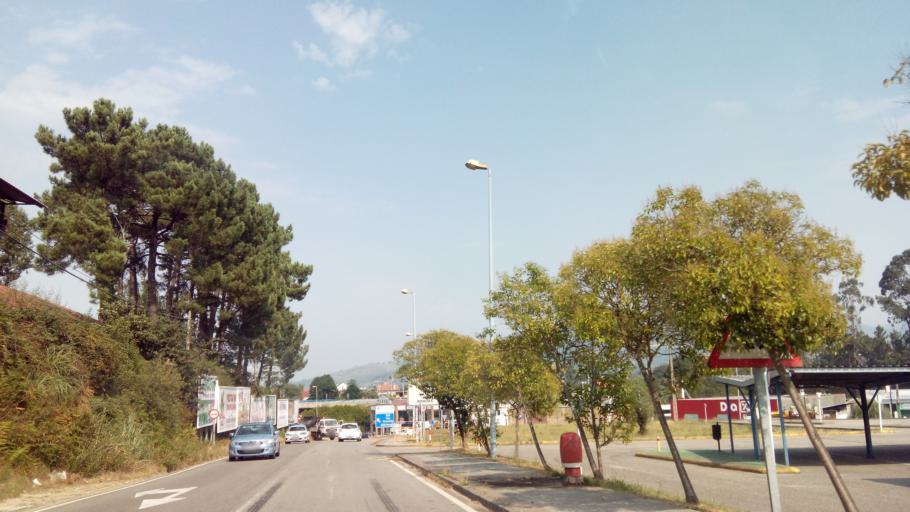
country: PT
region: Viana do Castelo
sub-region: Valenca
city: Valenca
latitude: 42.0372
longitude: -8.6603
